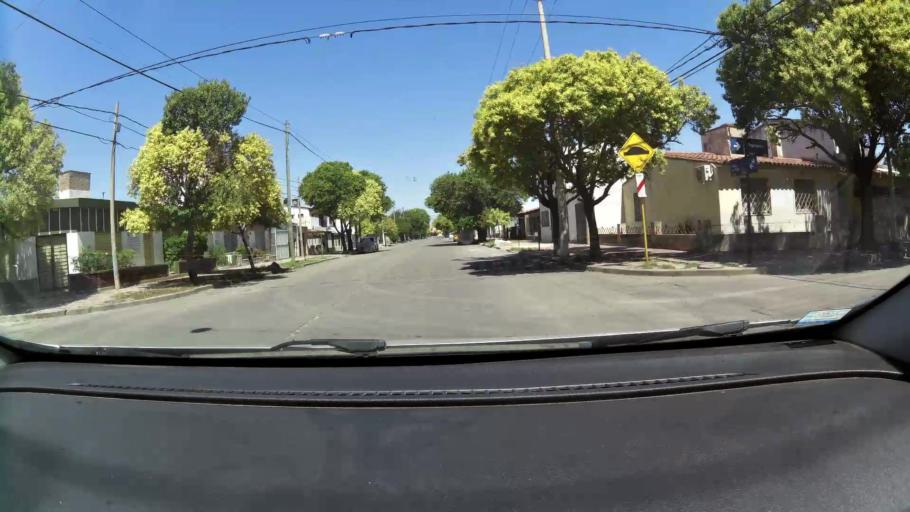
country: AR
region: Cordoba
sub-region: Departamento de Capital
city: Cordoba
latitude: -31.3848
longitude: -64.1624
